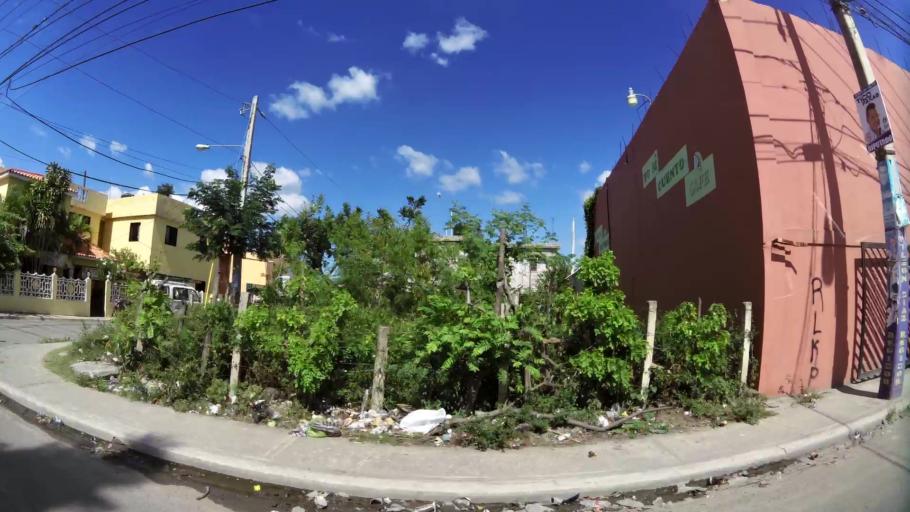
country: DO
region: San Cristobal
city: San Cristobal
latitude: 18.4232
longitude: -70.0978
